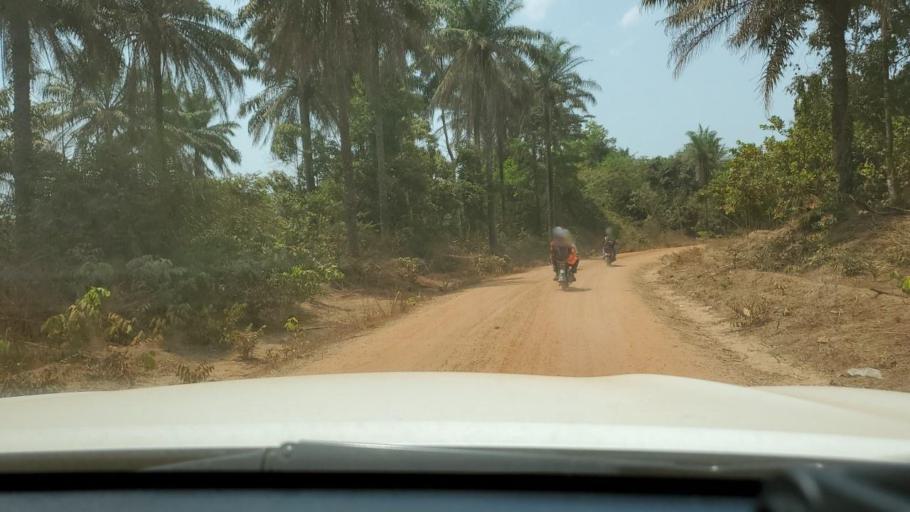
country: GN
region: Boke
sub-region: Boffa
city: Boffa
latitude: 10.0513
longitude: -13.8734
